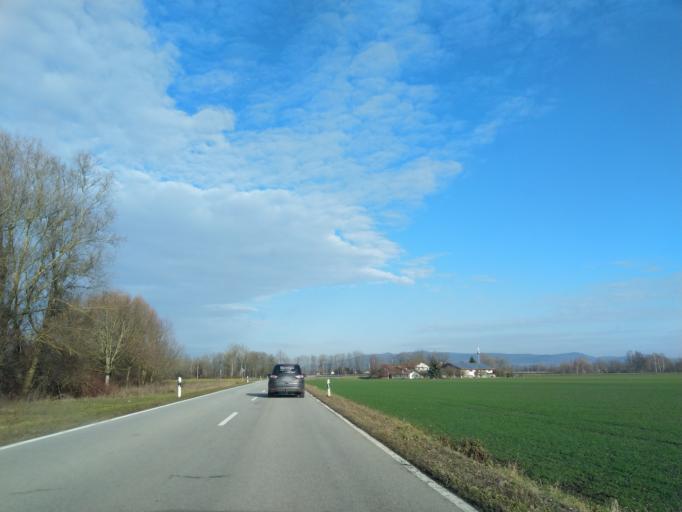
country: DE
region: Bavaria
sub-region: Lower Bavaria
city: Aholming
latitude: 48.7535
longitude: 12.9047
